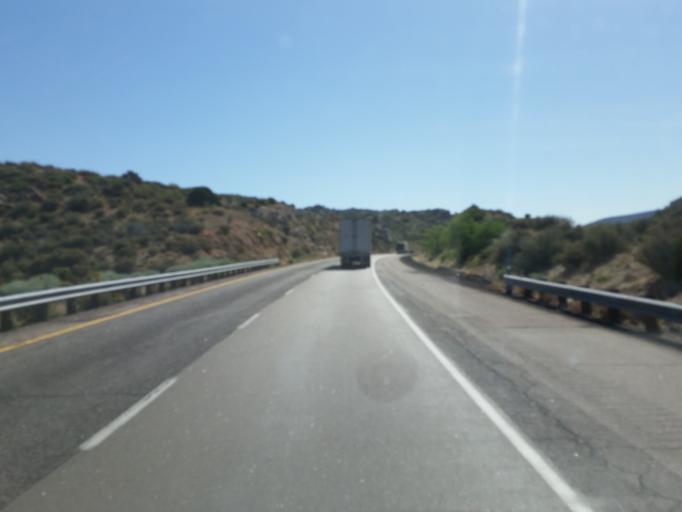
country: US
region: Arizona
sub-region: Mohave County
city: Peach Springs
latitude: 35.1767
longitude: -113.4905
